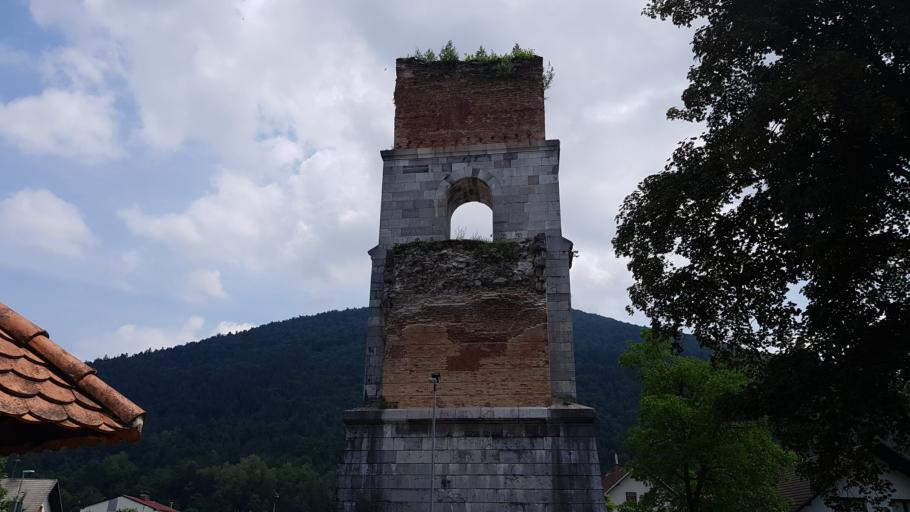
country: SI
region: Borovnica
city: Borovnica
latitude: 45.9192
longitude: 14.3642
